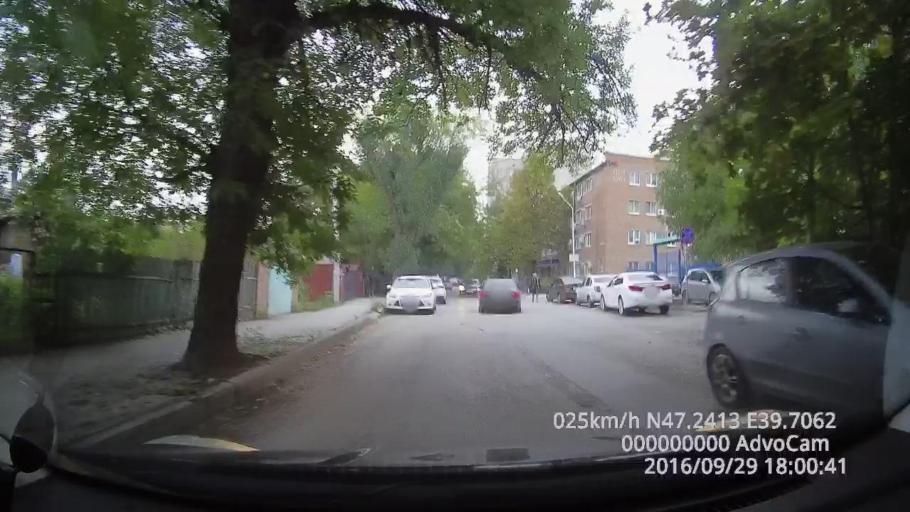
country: RU
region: Rostov
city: Rostov-na-Donu
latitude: 47.2413
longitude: 39.7064
